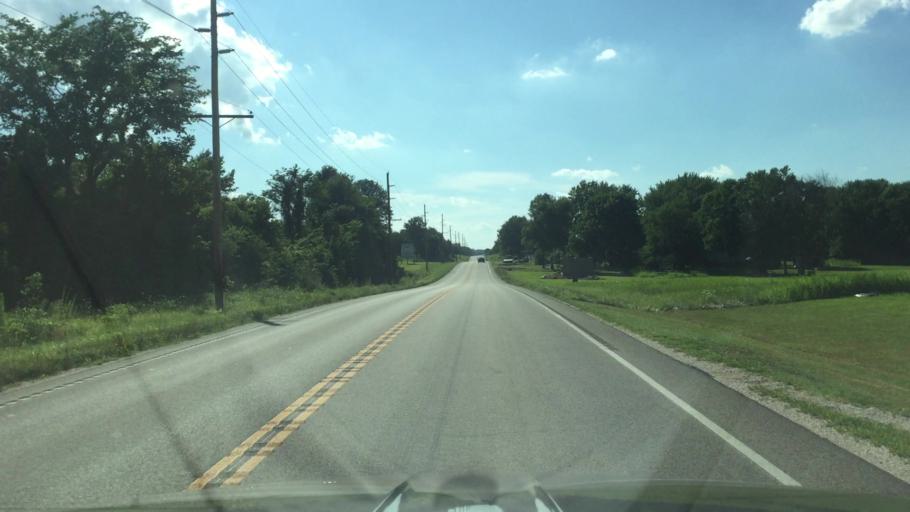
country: US
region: Missouri
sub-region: Morgan County
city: Versailles
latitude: 38.3974
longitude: -92.7287
